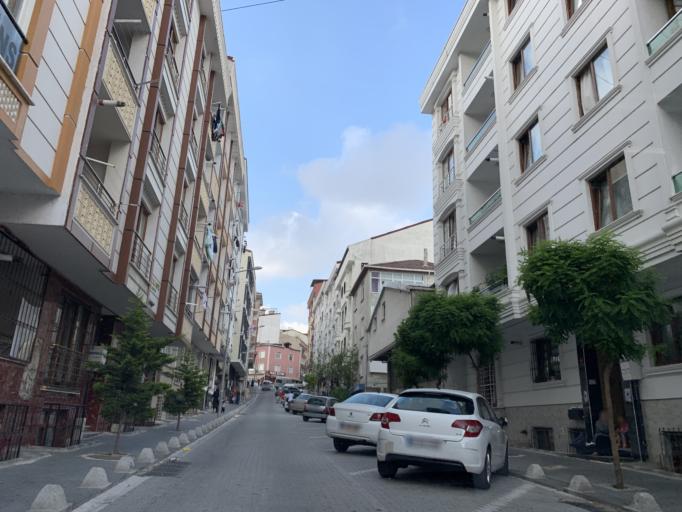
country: TR
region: Istanbul
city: Esenyurt
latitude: 41.0239
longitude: 28.6746
